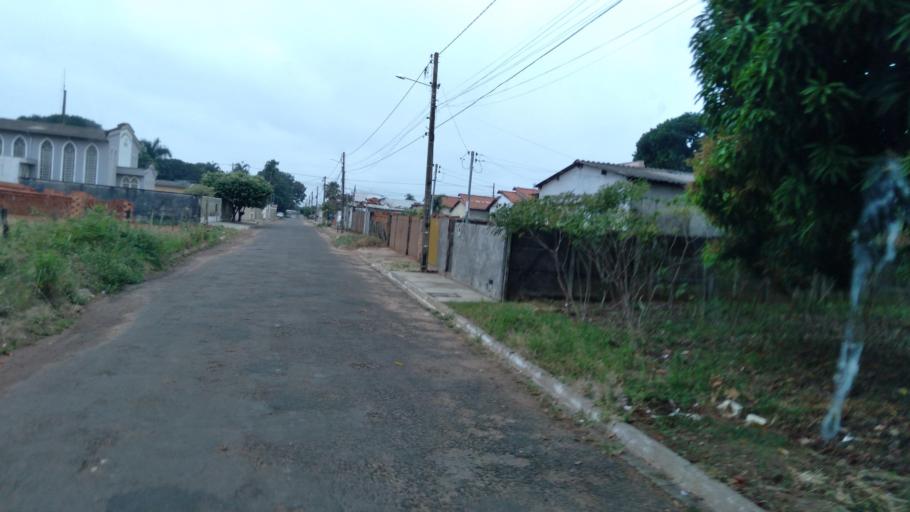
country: BR
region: Goias
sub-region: Mineiros
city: Mineiros
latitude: -17.5802
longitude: -52.5467
